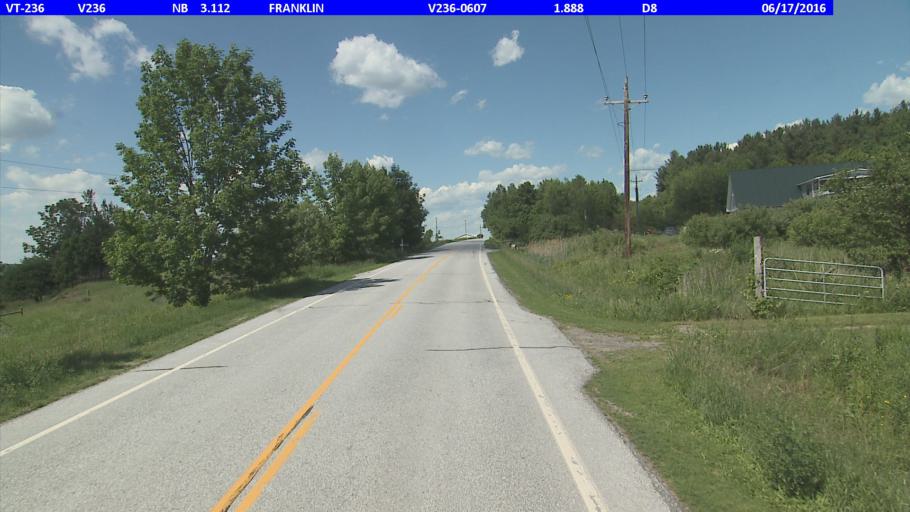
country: US
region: Vermont
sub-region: Franklin County
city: Enosburg Falls
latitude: 44.9550
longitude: -72.8616
